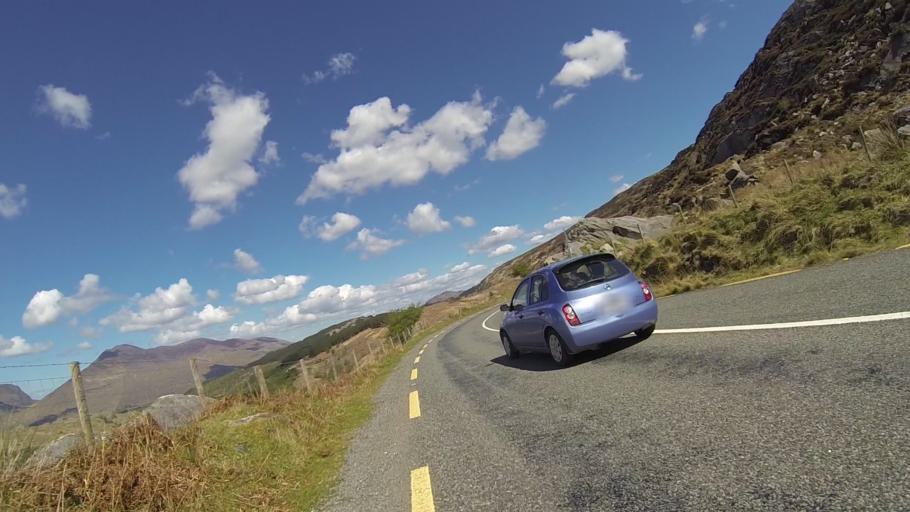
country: IE
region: Munster
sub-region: Ciarrai
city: Kenmare
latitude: 51.9462
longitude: -9.6400
